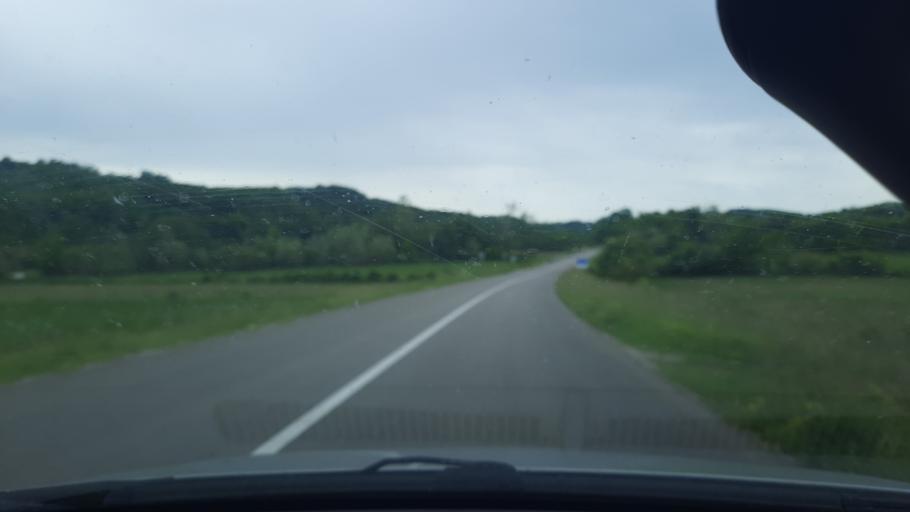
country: RS
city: Bukor
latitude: 44.5283
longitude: 19.5146
